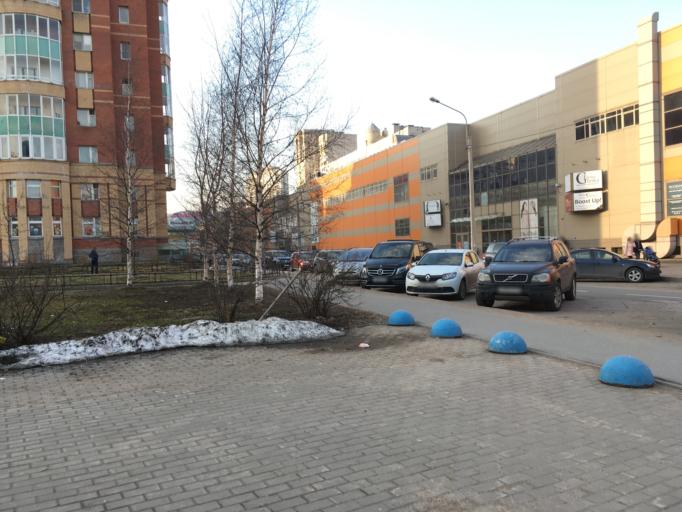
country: RU
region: St.-Petersburg
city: Komendantsky aerodrom
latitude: 60.0037
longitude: 30.2635
